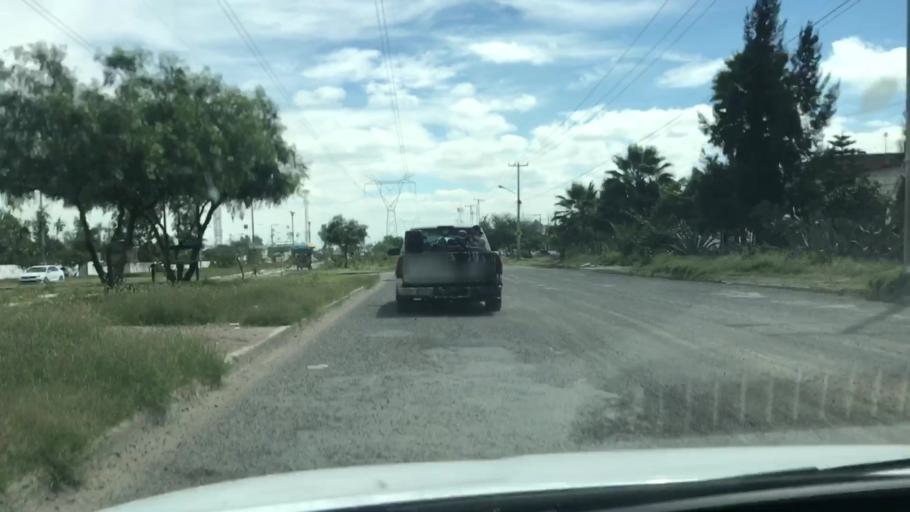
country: MX
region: Guanajuato
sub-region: Celaya
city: La Trinidad
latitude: 20.5491
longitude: -100.7890
